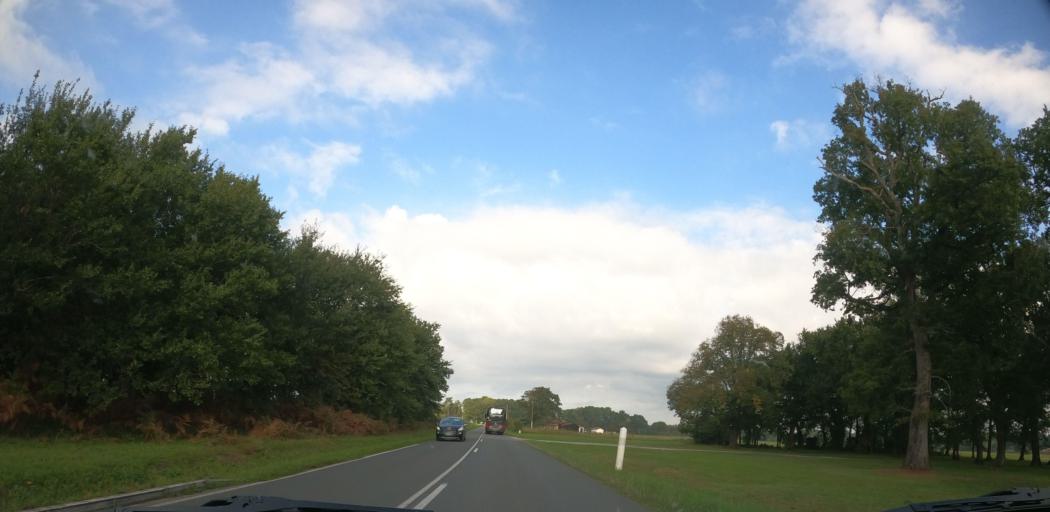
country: FR
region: Aquitaine
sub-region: Departement des Landes
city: Soustons
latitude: 43.7433
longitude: -1.3006
